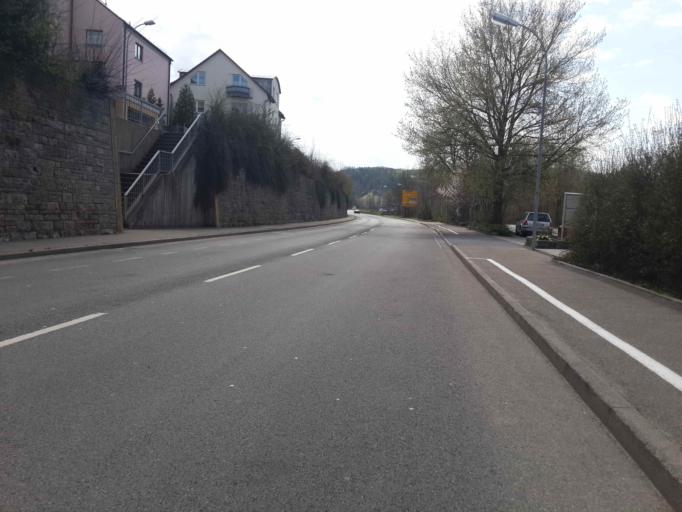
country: DE
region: Baden-Wuerttemberg
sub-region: Regierungsbezirk Stuttgart
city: Bad Mergentheim
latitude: 49.4832
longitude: 9.7700
